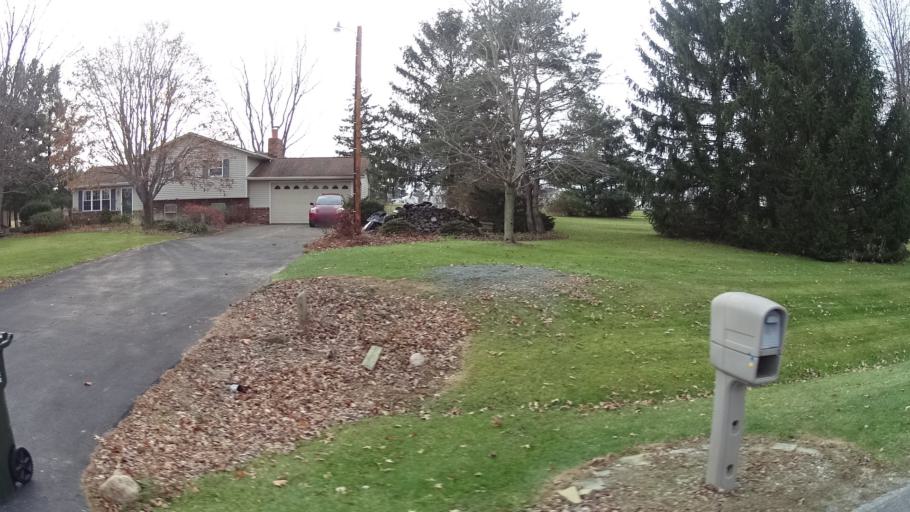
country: US
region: Ohio
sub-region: Lorain County
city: Lagrange
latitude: 41.2179
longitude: -82.0916
